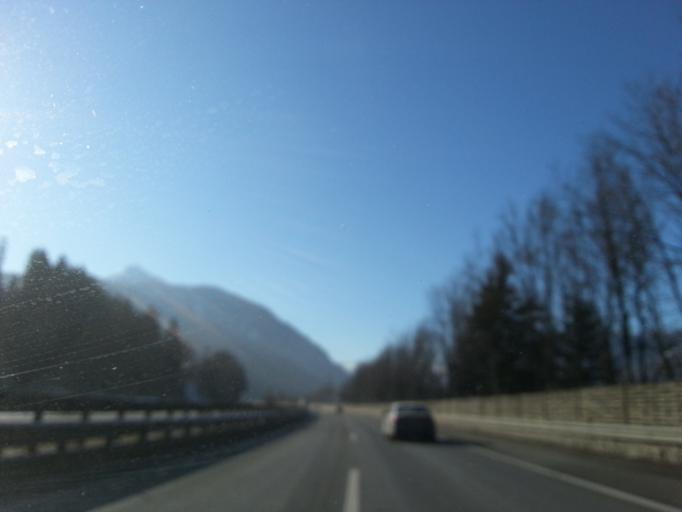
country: AT
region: Salzburg
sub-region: Politischer Bezirk Sankt Johann im Pongau
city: Altenmarkt im Pongau
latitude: 47.3702
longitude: 13.3945
